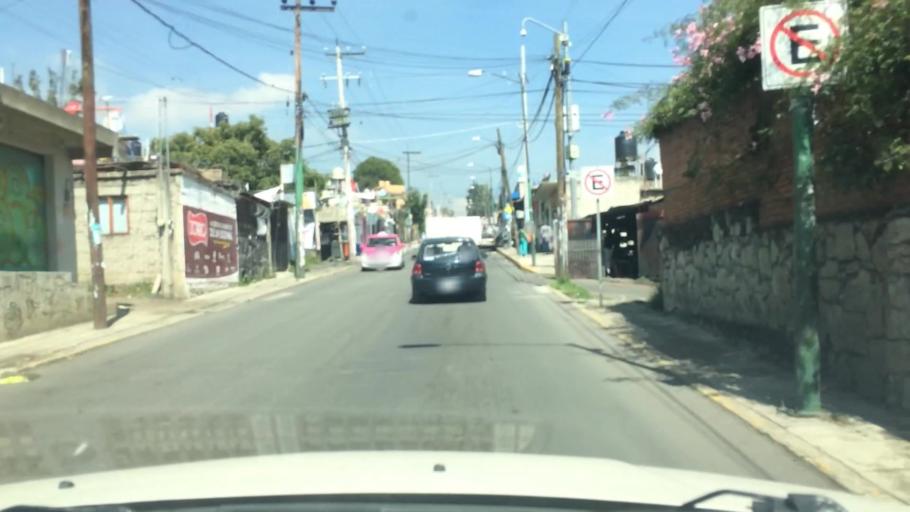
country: MX
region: Mexico City
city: Xochimilco
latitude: 19.2341
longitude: -99.1602
